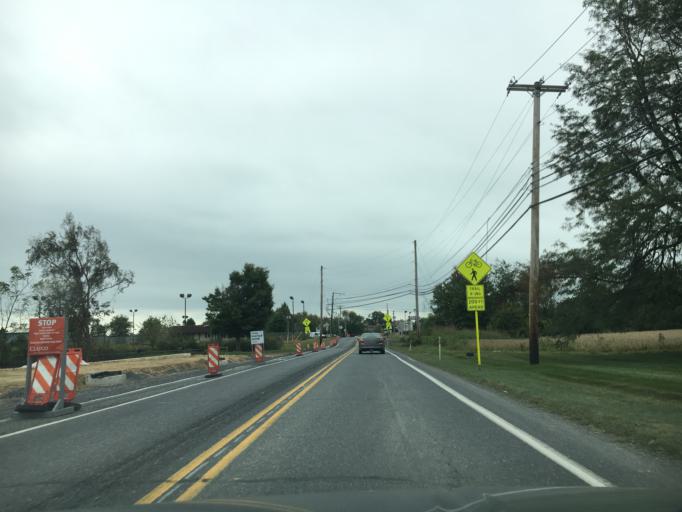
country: US
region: Pennsylvania
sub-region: Northampton County
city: Bath
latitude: 40.7010
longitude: -75.4177
